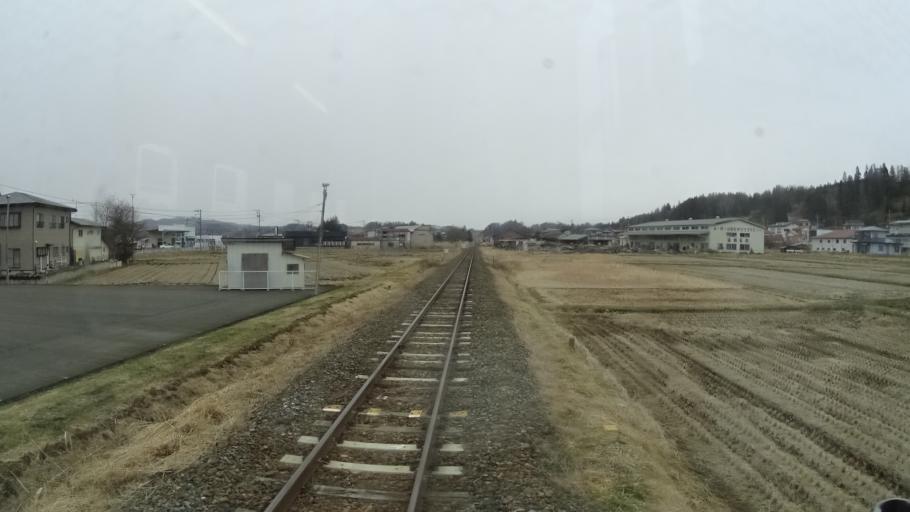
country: JP
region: Iwate
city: Hanamaki
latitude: 39.3808
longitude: 141.2365
